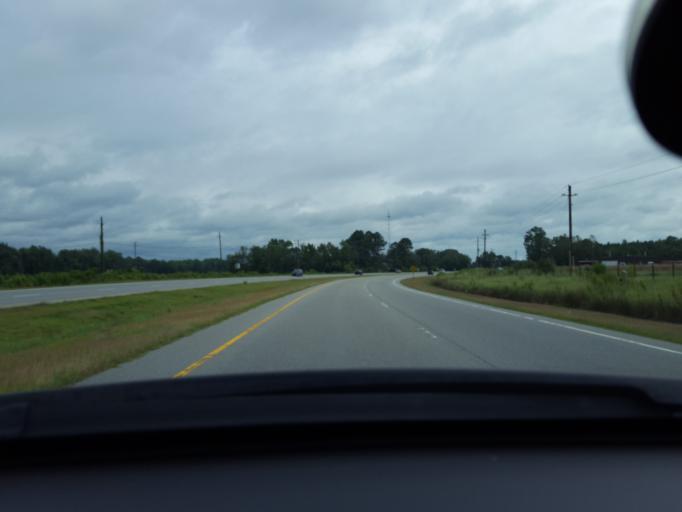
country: US
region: North Carolina
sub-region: Pitt County
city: Ayden
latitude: 35.4532
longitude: -77.4306
